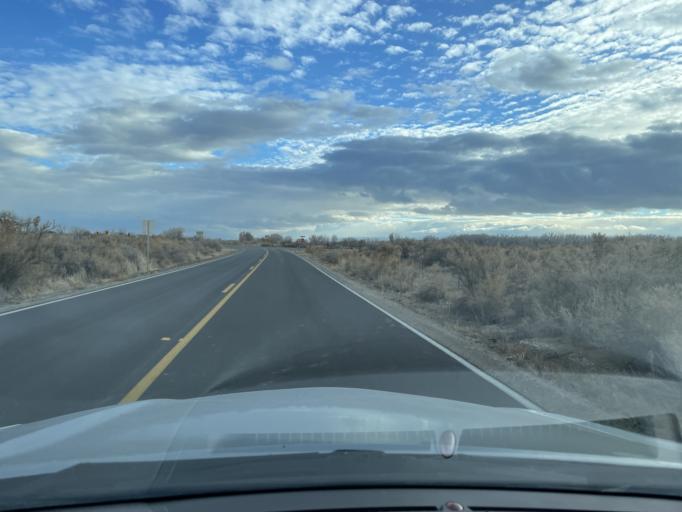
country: US
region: Colorado
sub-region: Montrose County
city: Olathe
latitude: 38.6434
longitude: -107.9937
